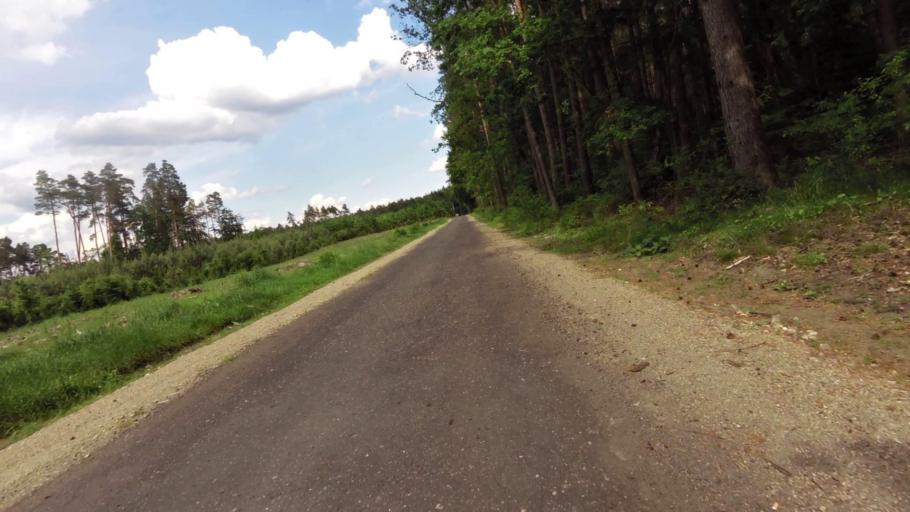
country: PL
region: West Pomeranian Voivodeship
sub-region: Powiat mysliborski
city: Debno
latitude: 52.7982
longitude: 14.6490
